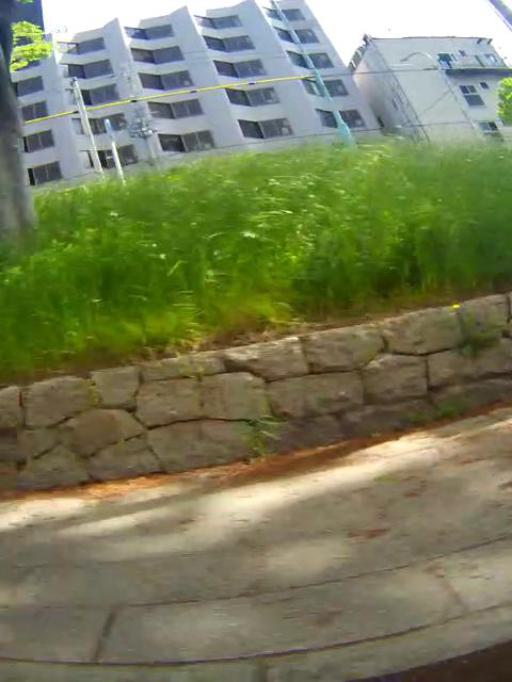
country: JP
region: Osaka
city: Osaka-shi
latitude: 34.7016
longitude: 135.5224
